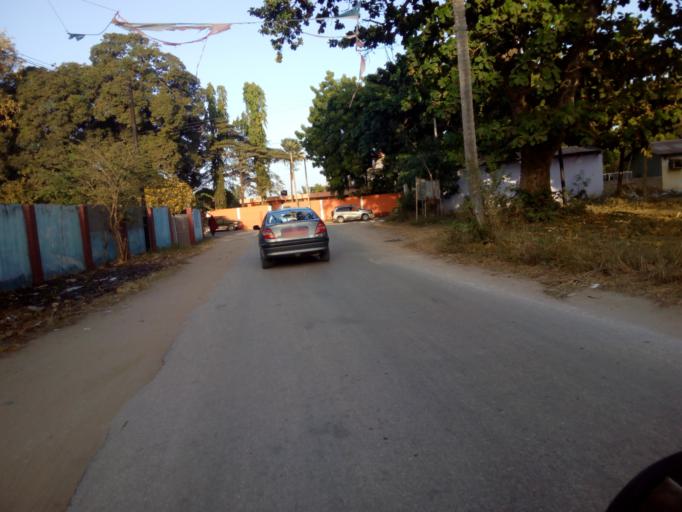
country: TZ
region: Zanzibar Urban/West
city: Zanzibar
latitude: -6.2065
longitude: 39.2095
